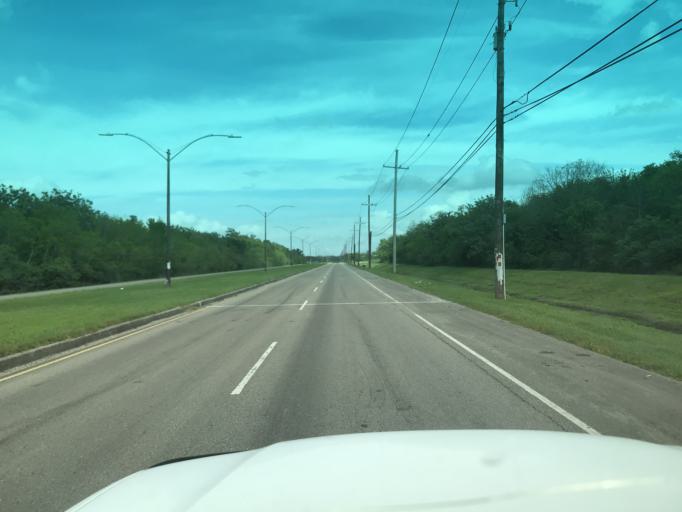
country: US
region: Louisiana
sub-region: Saint Bernard Parish
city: Arabi
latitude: 30.0058
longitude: -90.0049
